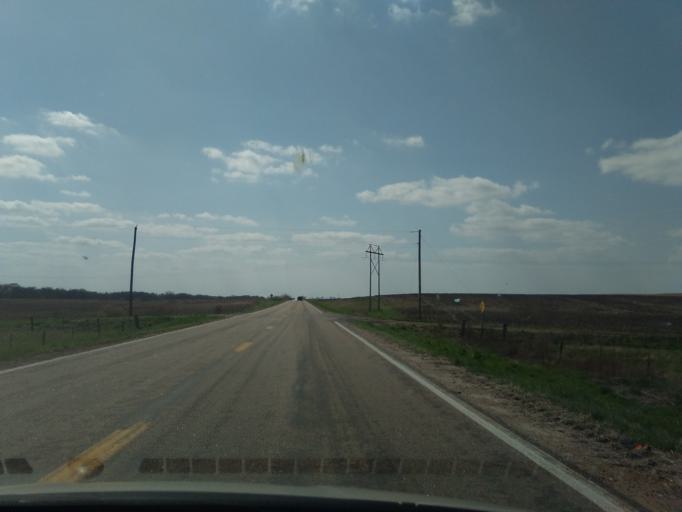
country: US
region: Nebraska
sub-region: Thayer County
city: Hebron
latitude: 40.1472
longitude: -97.6131
